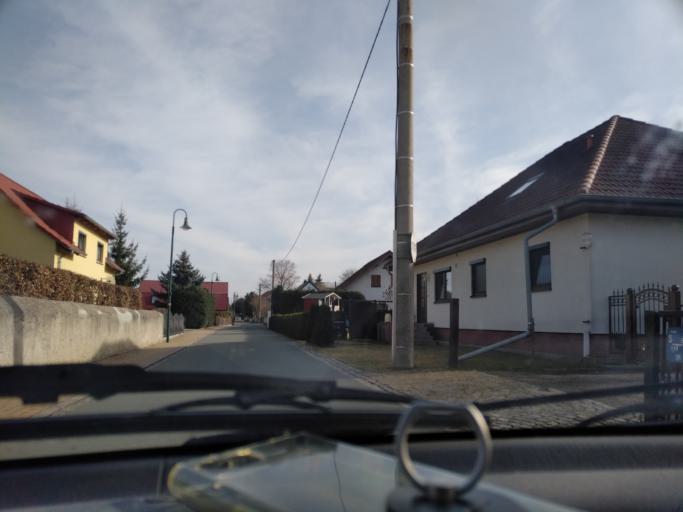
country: DE
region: Saxony
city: Glaubitz
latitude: 51.3134
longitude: 13.3718
